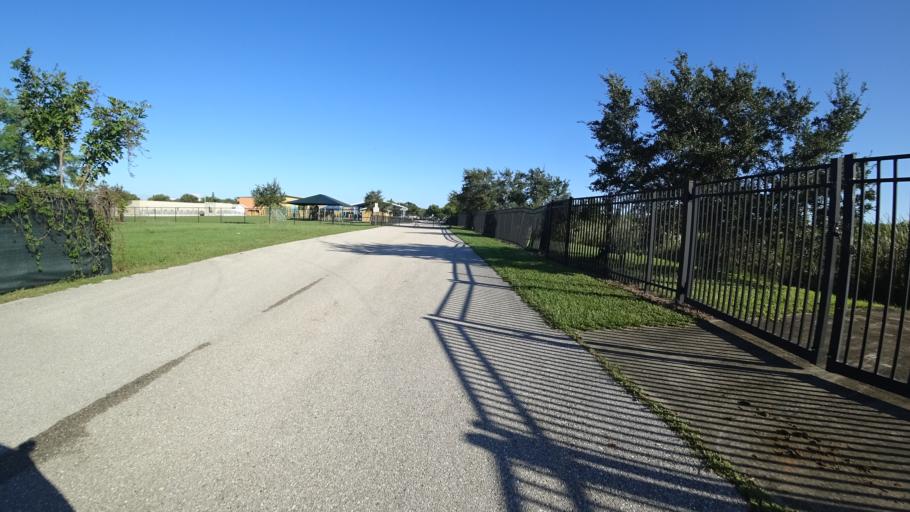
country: US
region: Florida
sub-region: Manatee County
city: Bradenton
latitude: 27.4851
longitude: -82.5670
